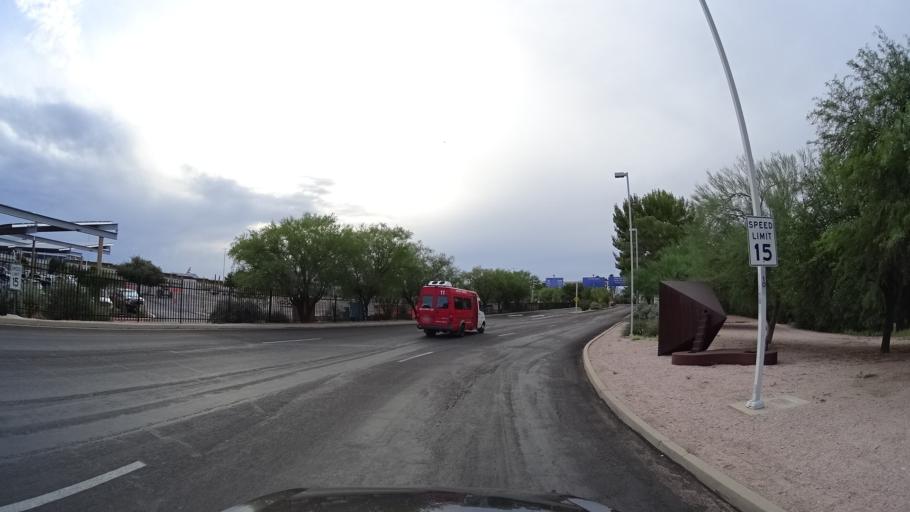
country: US
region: Arizona
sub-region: Pima County
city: Summit
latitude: 32.1227
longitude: -110.9363
